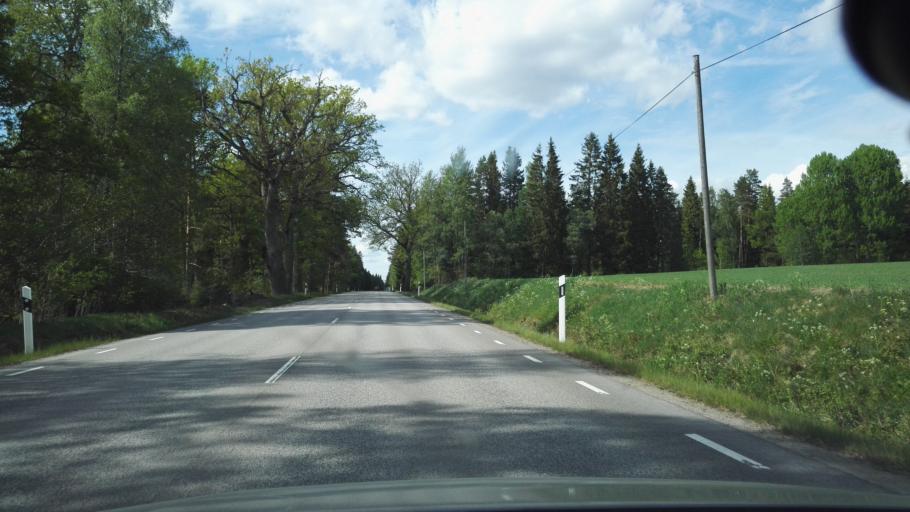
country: SE
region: Kronoberg
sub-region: Vaxjo Kommun
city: Braas
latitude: 57.0479
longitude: 15.0623
